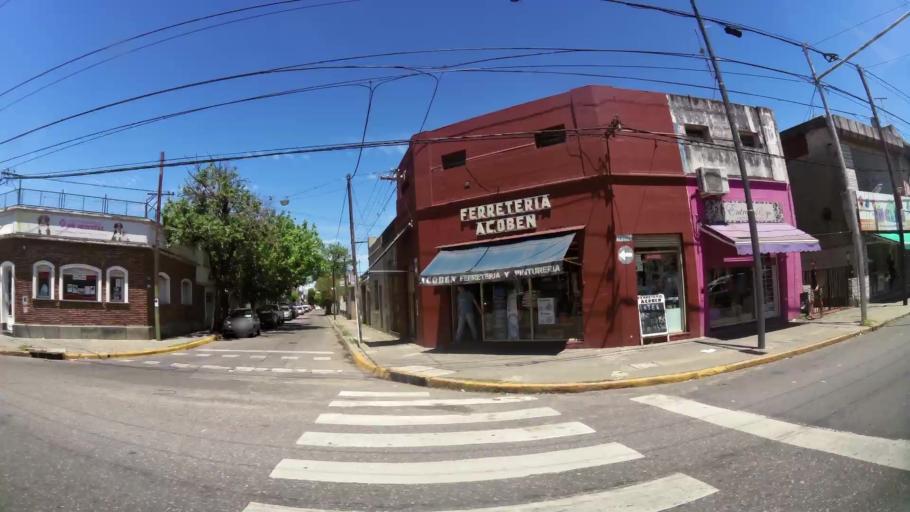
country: AR
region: Santa Fe
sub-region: Departamento de Rosario
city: Rosario
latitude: -32.9409
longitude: -60.6987
